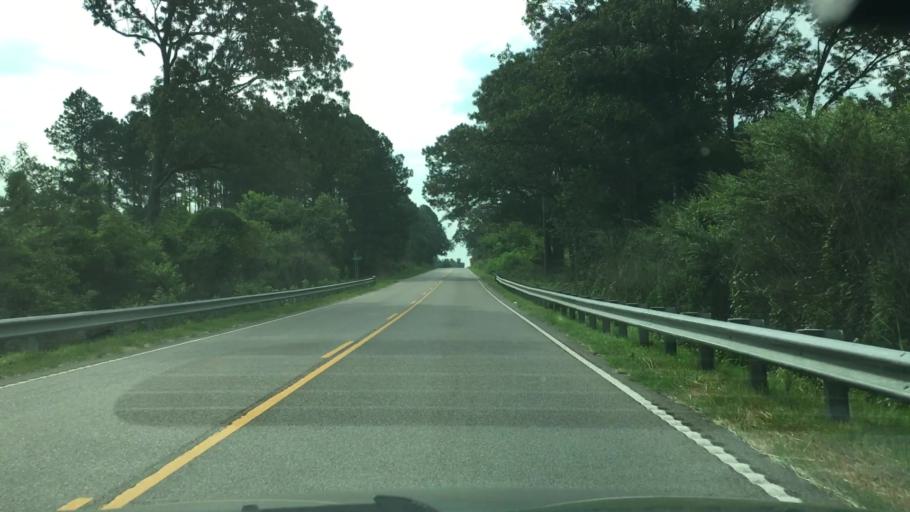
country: US
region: South Carolina
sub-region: Lexington County
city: Leesville
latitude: 33.6864
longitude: -81.4587
